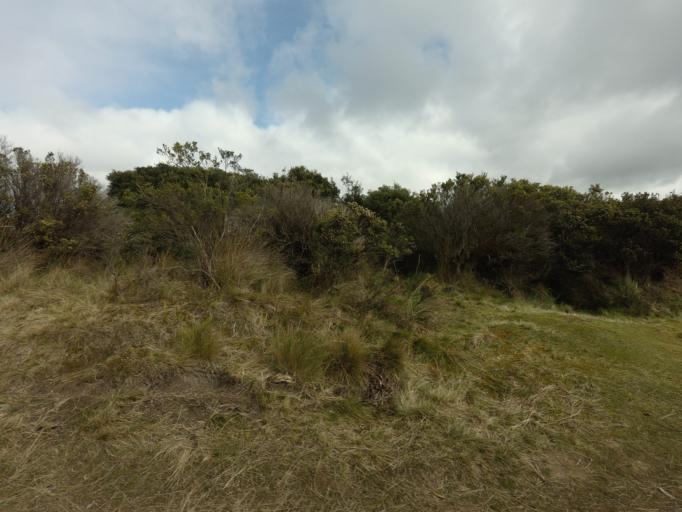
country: AU
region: Tasmania
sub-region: Huon Valley
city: Geeveston
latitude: -43.5814
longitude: 146.8970
